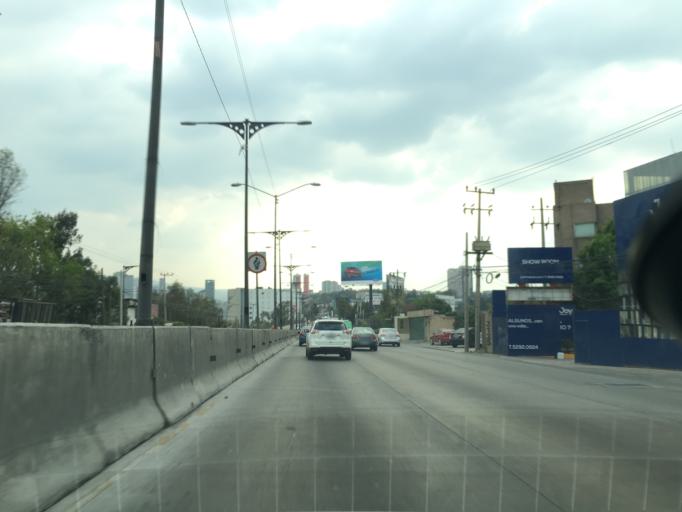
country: MX
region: Mexico City
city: Col. Bosques de las Lomas
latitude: 19.3778
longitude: -99.2591
